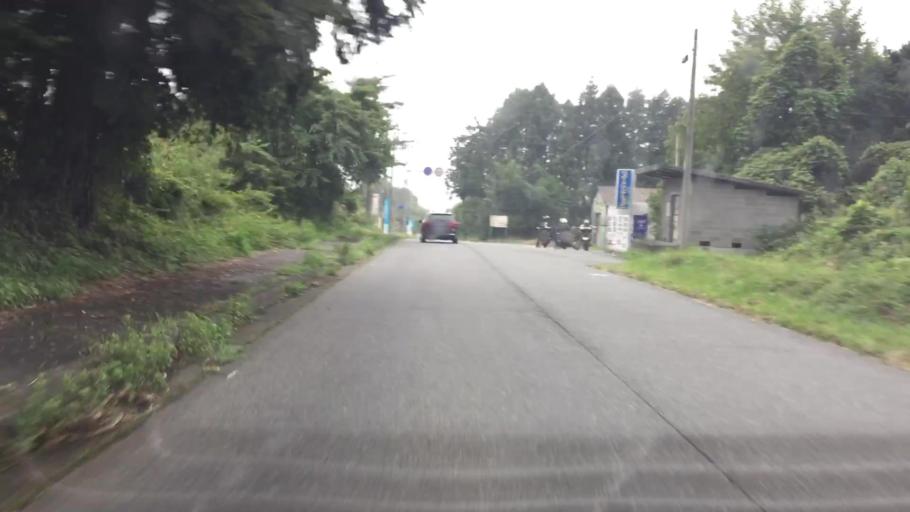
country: JP
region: Shizuoka
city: Fujinomiya
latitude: 35.3463
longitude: 138.5956
